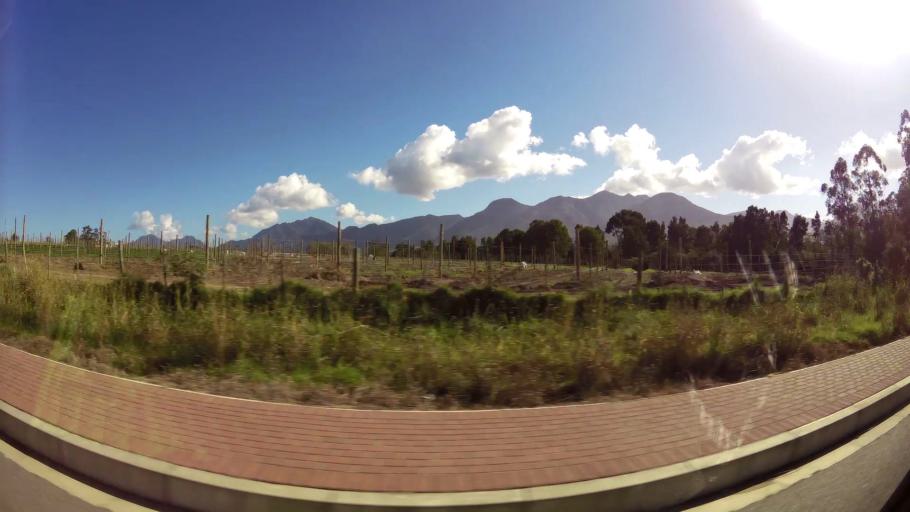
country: ZA
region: Western Cape
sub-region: Eden District Municipality
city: George
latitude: -33.9527
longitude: 22.4016
